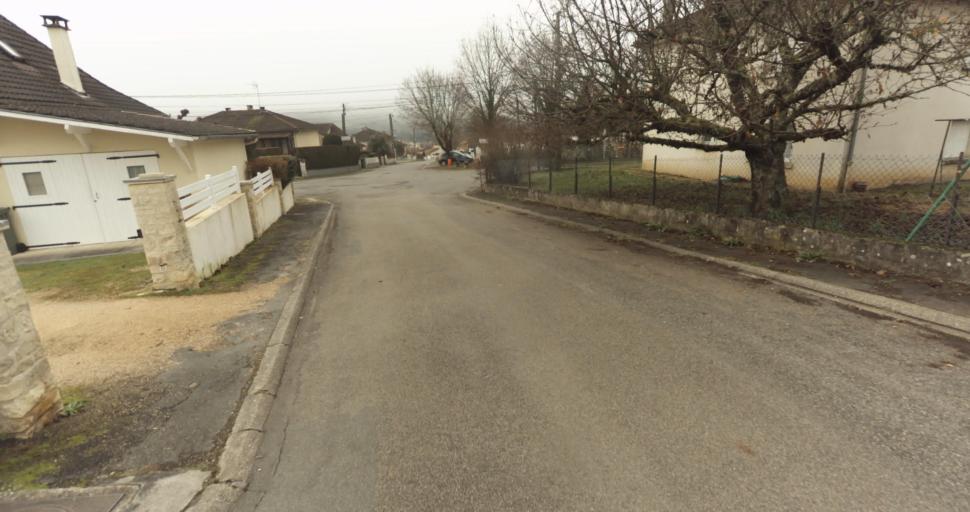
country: FR
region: Midi-Pyrenees
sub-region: Departement du Lot
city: Figeac
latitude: 44.6120
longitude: 2.0437
